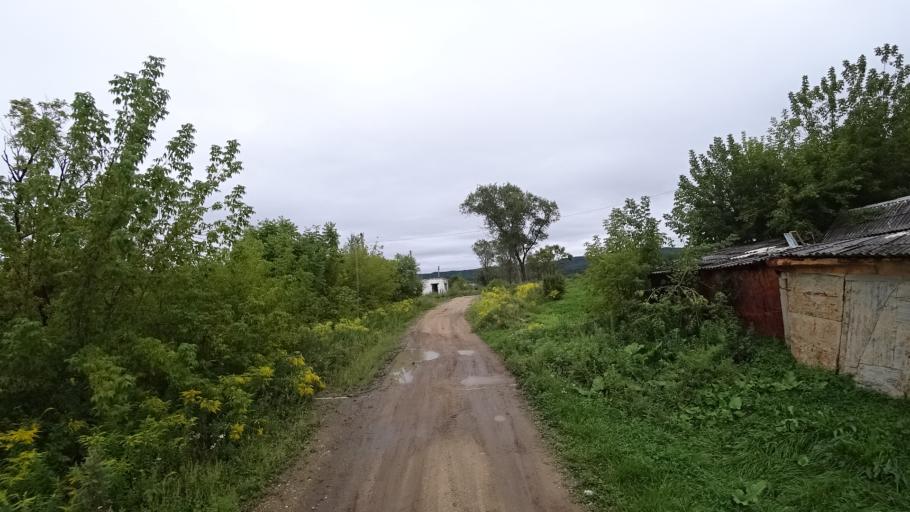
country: RU
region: Primorskiy
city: Rettikhovka
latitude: 44.1589
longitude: 132.7445
